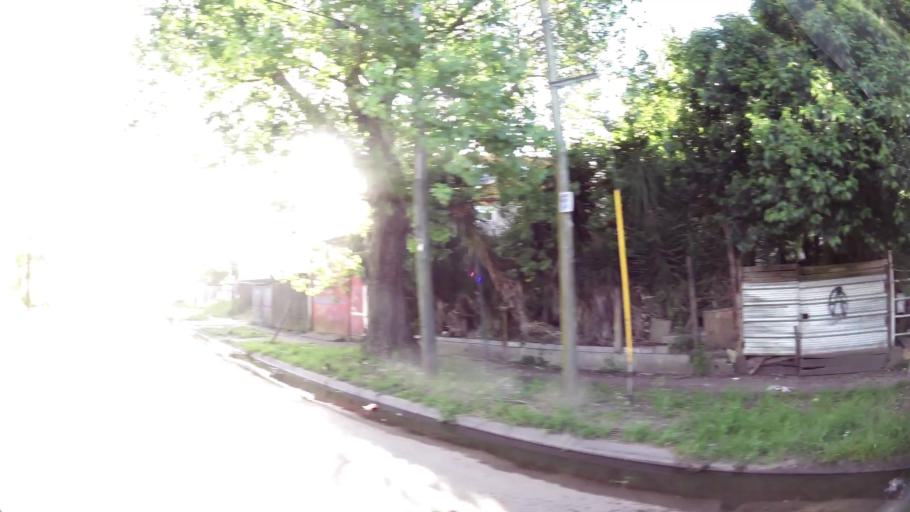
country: AR
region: Buenos Aires
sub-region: Partido de Almirante Brown
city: Adrogue
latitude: -34.8172
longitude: -58.3335
